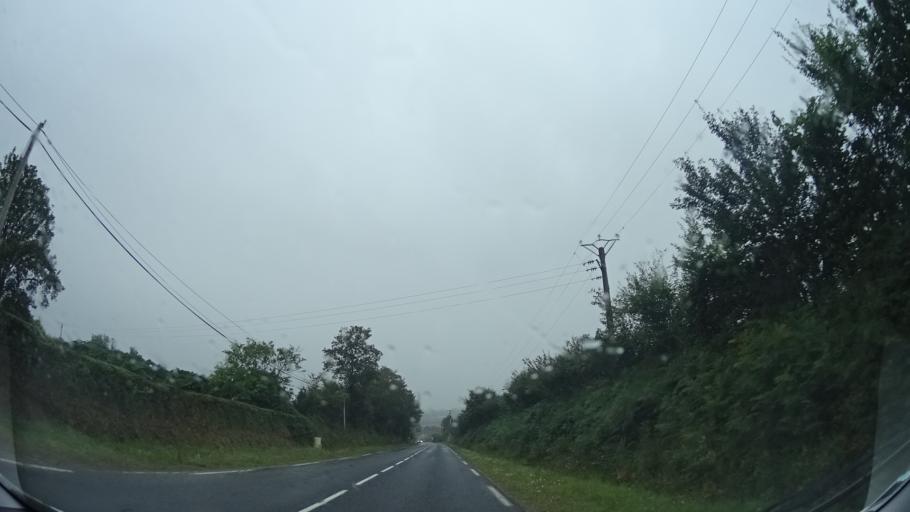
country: FR
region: Lower Normandy
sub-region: Departement de la Manche
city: Martinvast
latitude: 49.6133
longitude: -1.6997
